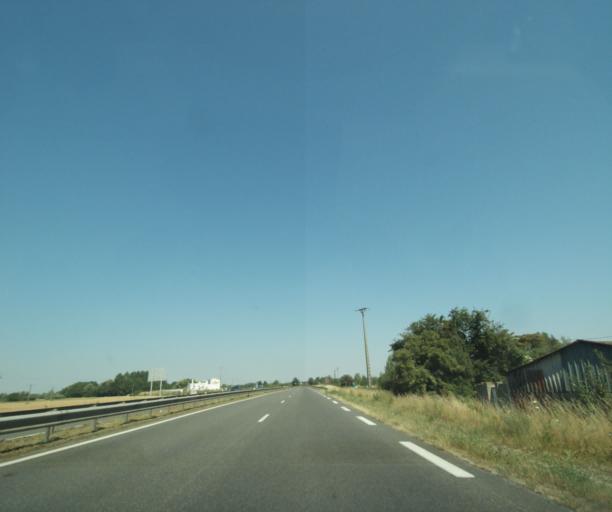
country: FR
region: Champagne-Ardenne
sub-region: Departement de la Haute-Marne
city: Villiers-en-Lieu
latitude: 48.6557
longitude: 4.8183
